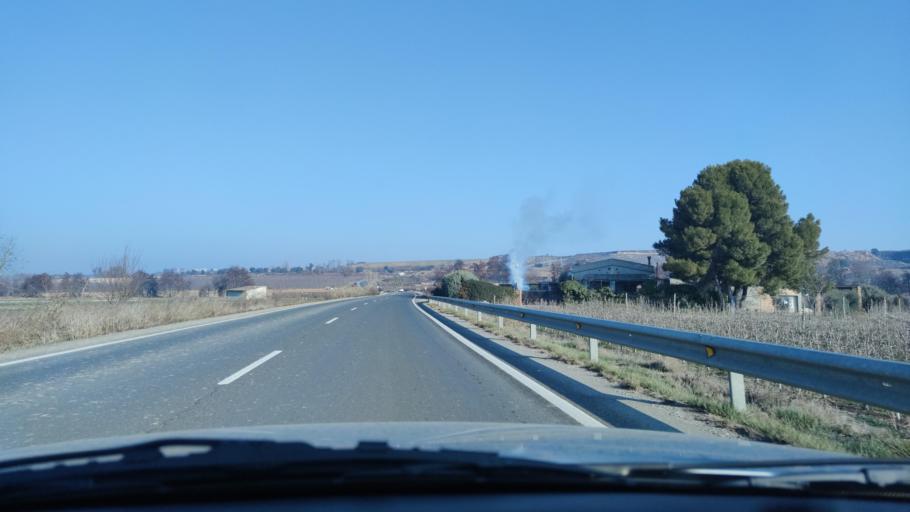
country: ES
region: Catalonia
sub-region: Provincia de Lleida
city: Albesa
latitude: 41.7214
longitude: 0.6400
